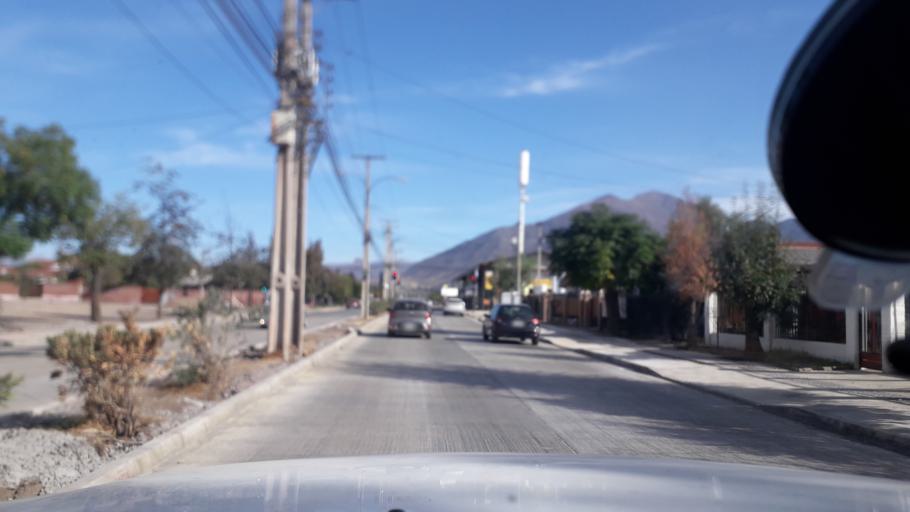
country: CL
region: Valparaiso
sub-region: Provincia de San Felipe
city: San Felipe
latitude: -32.7515
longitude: -70.7113
